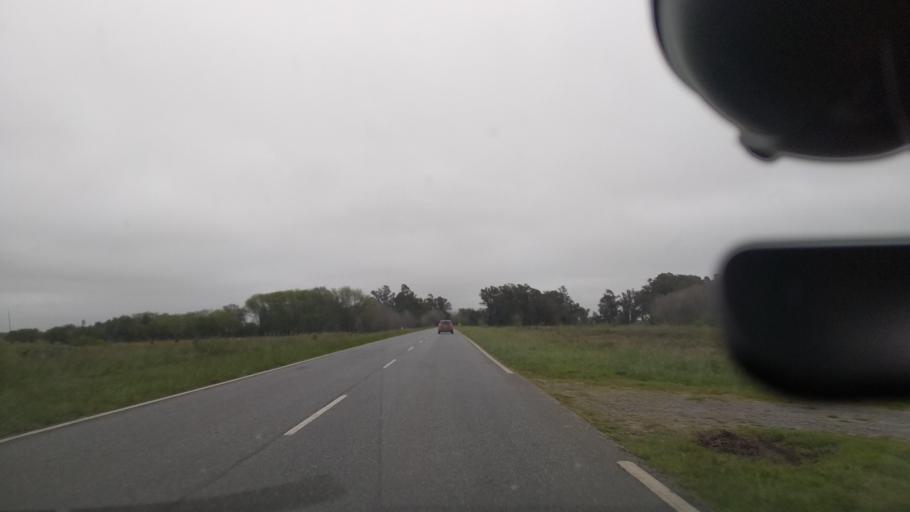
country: AR
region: Buenos Aires
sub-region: Partido de Magdalena
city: Magdalena
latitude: -35.2658
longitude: -57.6203
